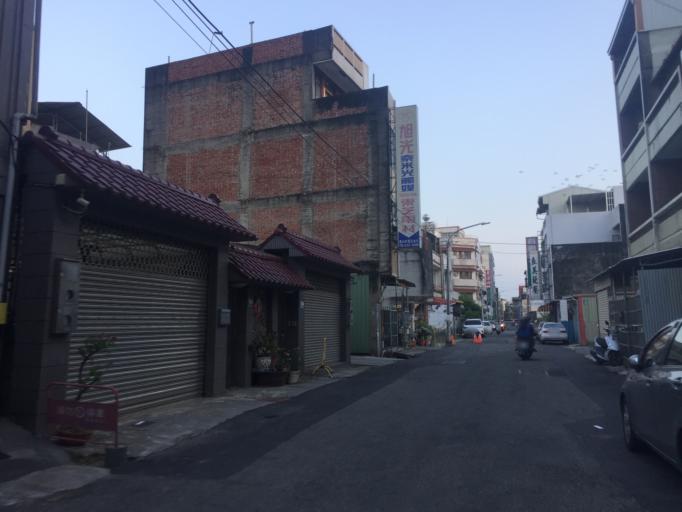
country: TW
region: Taiwan
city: Xinying
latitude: 23.3068
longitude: 120.3133
